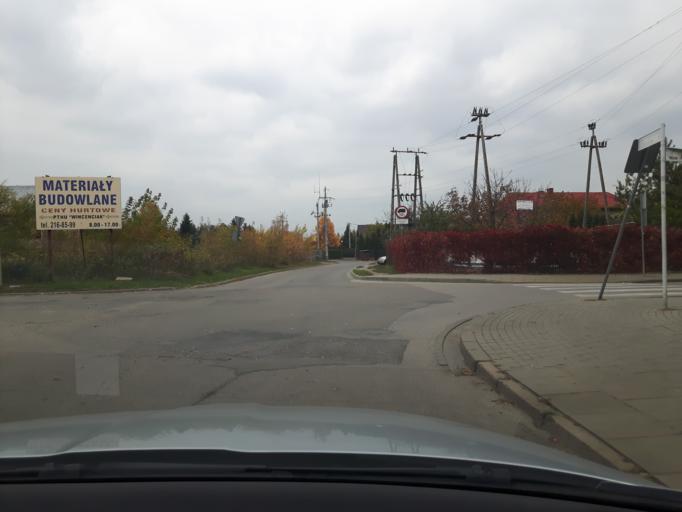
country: PL
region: Masovian Voivodeship
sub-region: Powiat wolominski
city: Zabki
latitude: 52.2880
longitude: 21.0949
